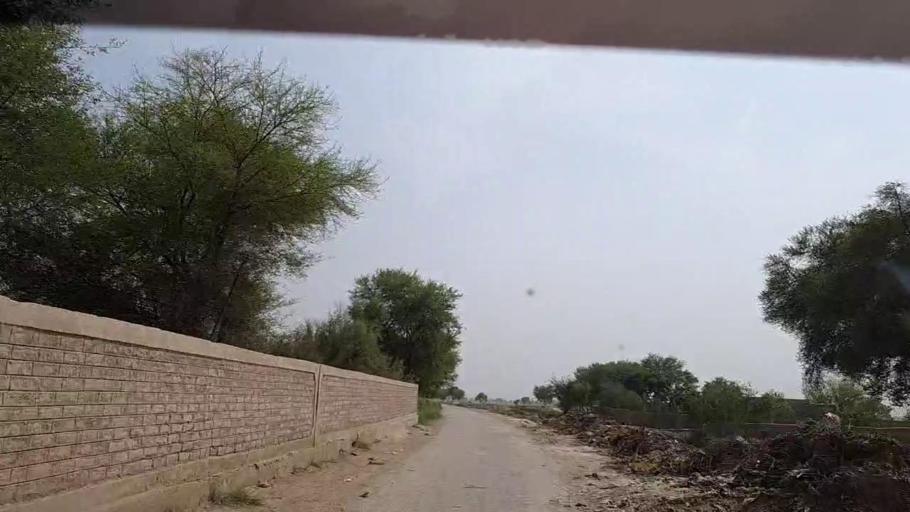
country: PK
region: Sindh
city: Khairpur Nathan Shah
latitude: 27.0758
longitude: 67.6885
